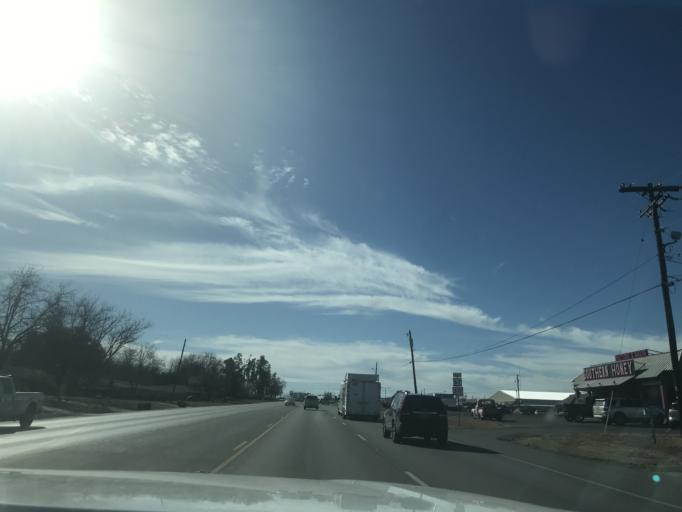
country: US
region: Texas
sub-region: Erath County
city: Stephenville
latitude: 32.2067
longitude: -98.2068
